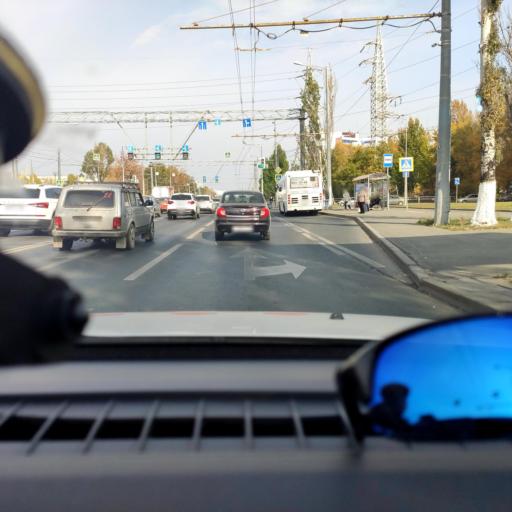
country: RU
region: Samara
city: Samara
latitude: 53.2397
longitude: 50.2059
